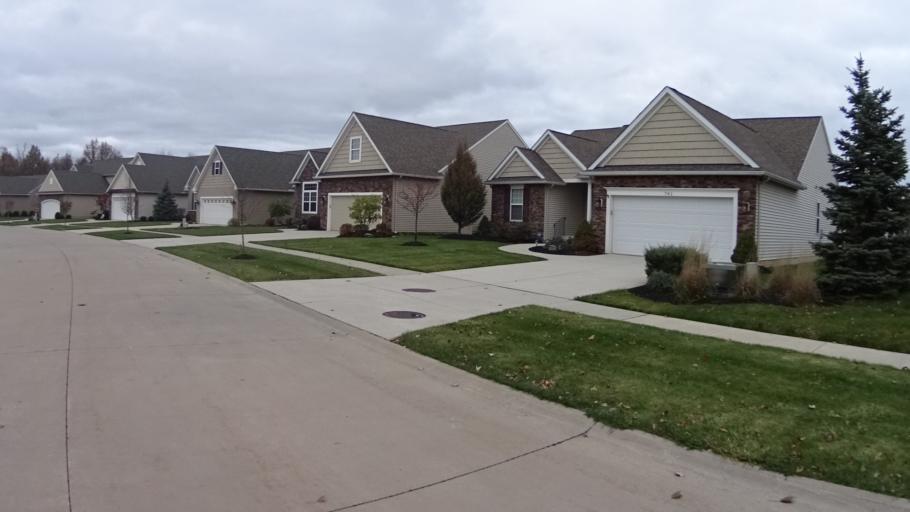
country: US
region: Ohio
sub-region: Lorain County
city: Avon Center
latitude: 41.4826
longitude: -81.9849
